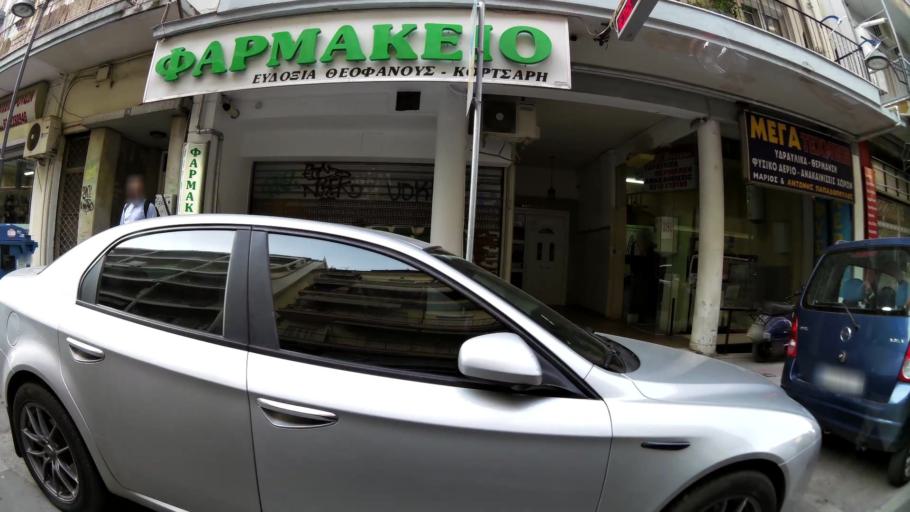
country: GR
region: Central Macedonia
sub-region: Nomos Thessalonikis
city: Agios Pavlos
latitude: 40.6385
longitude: 22.9500
